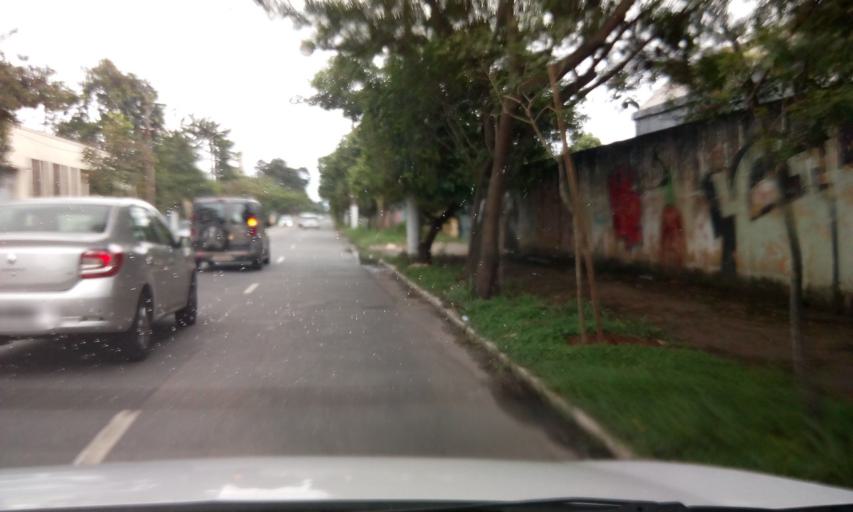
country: BR
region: Sao Paulo
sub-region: Sao Paulo
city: Sao Paulo
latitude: -23.5641
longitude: -46.6067
